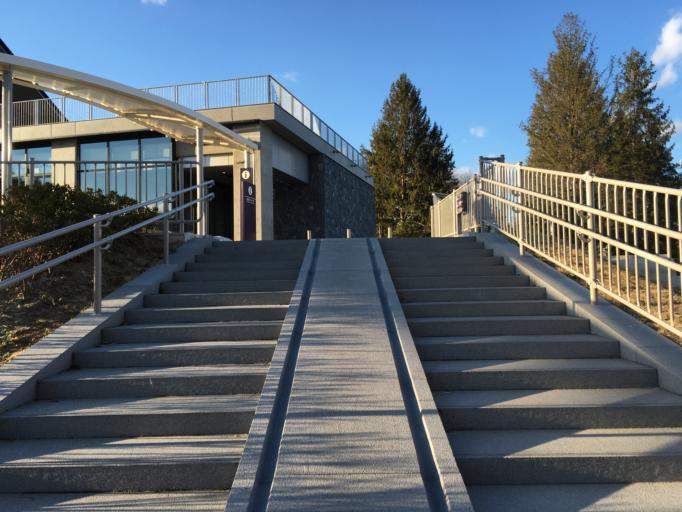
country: JP
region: Miyagi
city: Sendai
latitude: 38.2599
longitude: 140.8575
